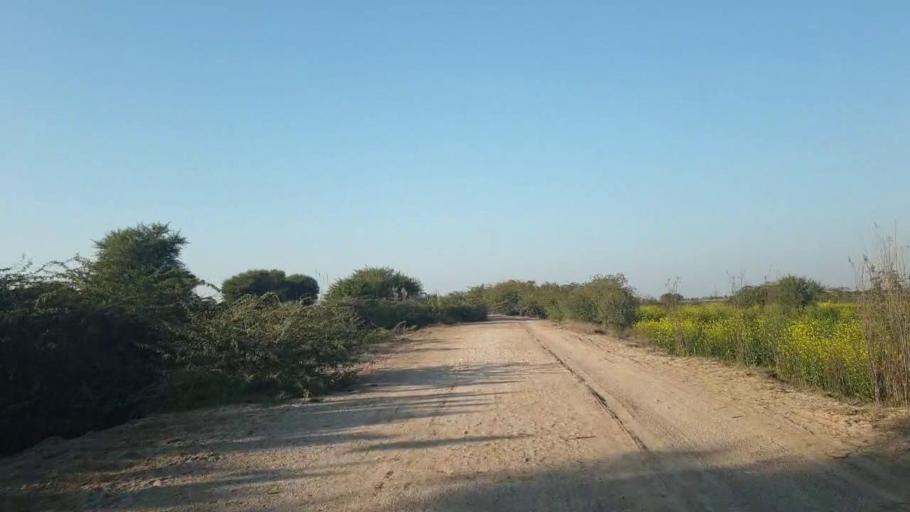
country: PK
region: Sindh
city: Shahpur Chakar
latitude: 26.0656
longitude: 68.6507
